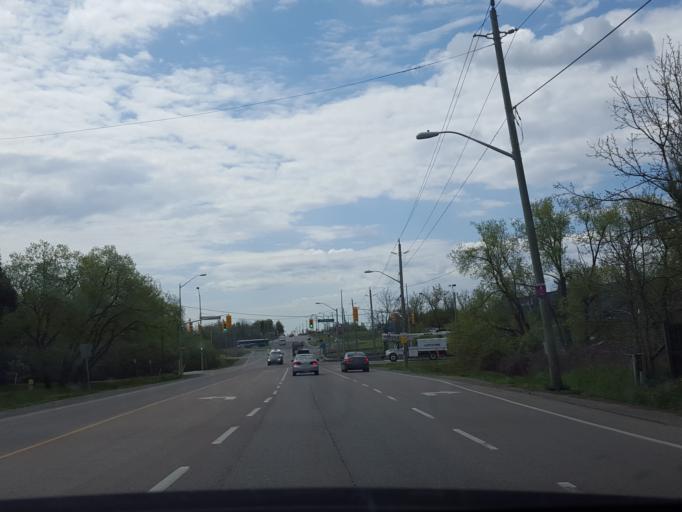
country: CA
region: Ontario
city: Oshawa
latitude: 43.9147
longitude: -78.7033
